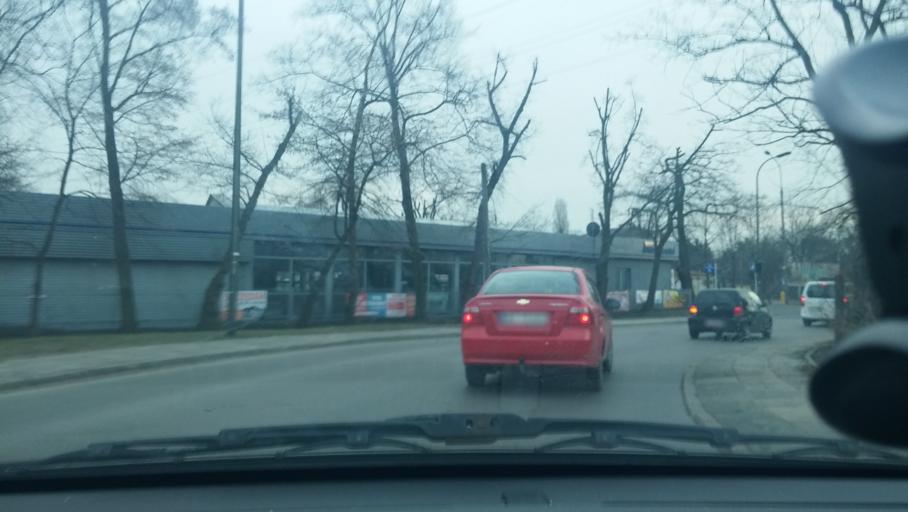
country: PL
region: Masovian Voivodeship
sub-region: Warszawa
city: Rembertow
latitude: 52.2255
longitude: 21.1495
